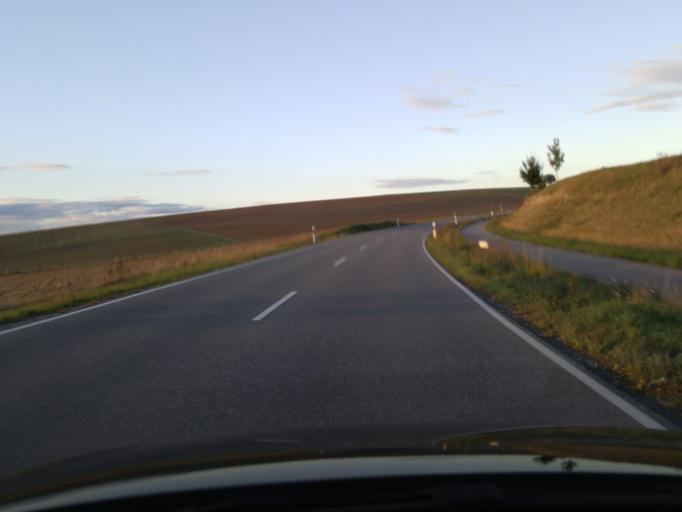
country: DE
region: Baden-Wuerttemberg
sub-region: Regierungsbezirk Stuttgart
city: Bad Rappenau
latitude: 49.2169
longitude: 9.1031
